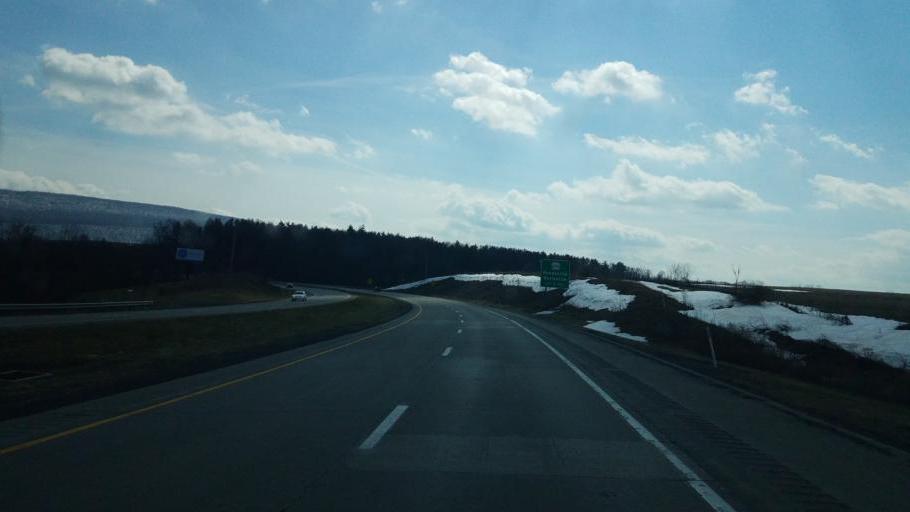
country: US
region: Pennsylvania
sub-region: Mifflin County
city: Church Hill
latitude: 40.6852
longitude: -77.6072
